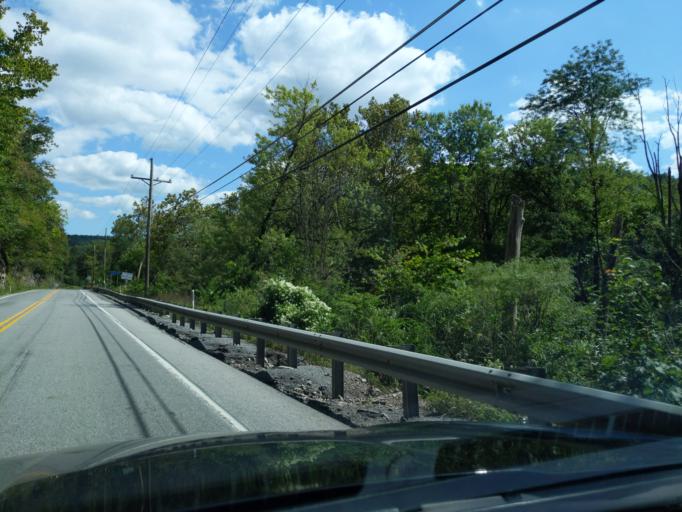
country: US
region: Pennsylvania
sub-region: Blair County
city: Tyrone
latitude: 40.6563
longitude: -78.2078
